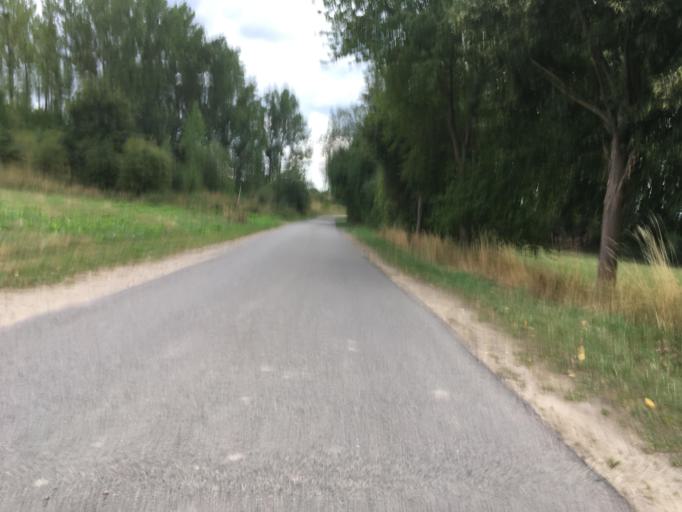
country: DE
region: Brandenburg
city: Prenzlau
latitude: 53.2561
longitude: 13.8813
